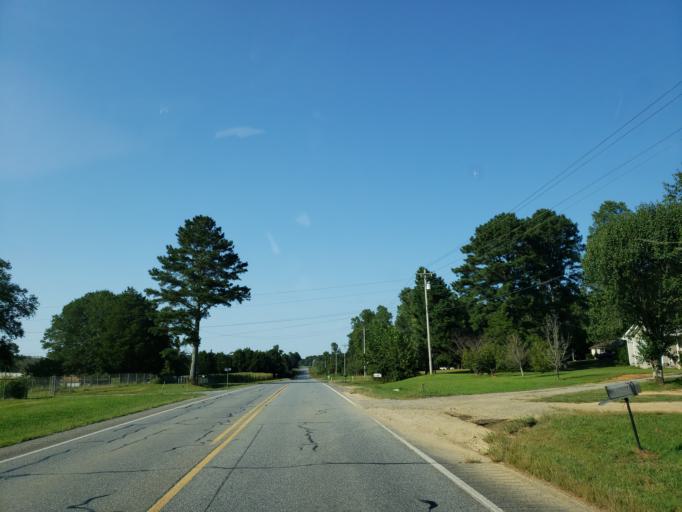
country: US
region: Tennessee
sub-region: Bradley County
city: Wildwood Lake
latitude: 34.9561
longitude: -84.7357
